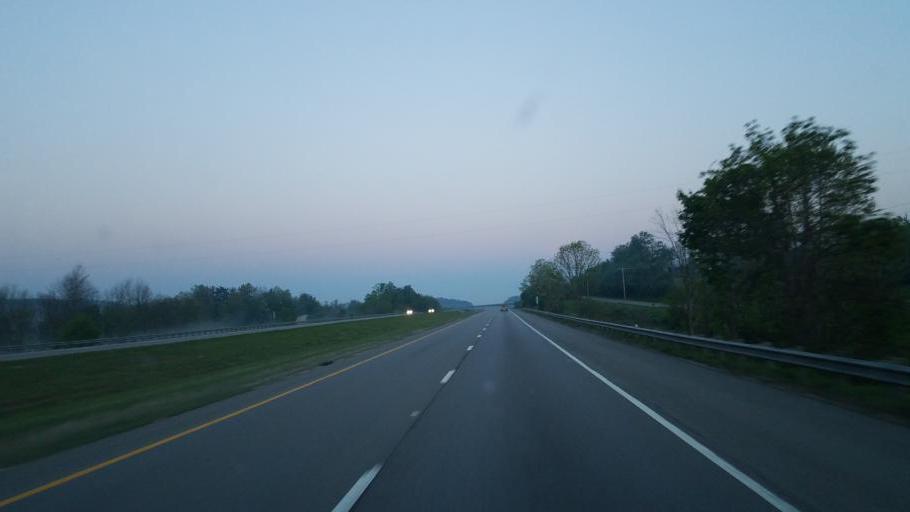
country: US
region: Ohio
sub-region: Belmont County
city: Barnesville
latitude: 40.0481
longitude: -81.3495
